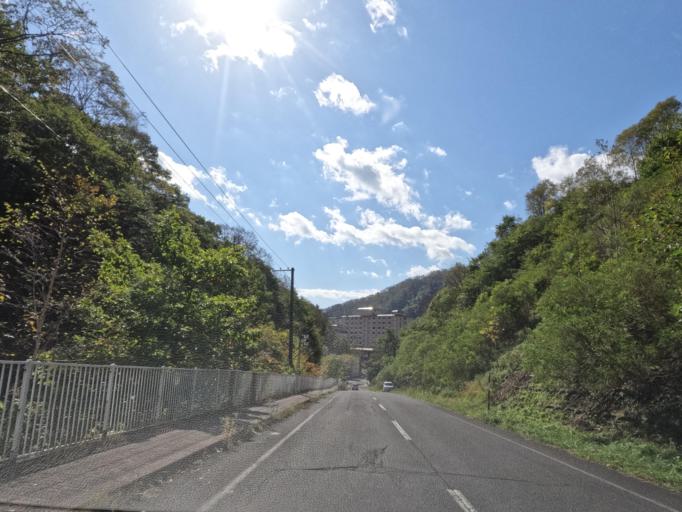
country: JP
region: Hokkaido
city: Shiraoi
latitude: 42.4984
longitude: 141.1413
